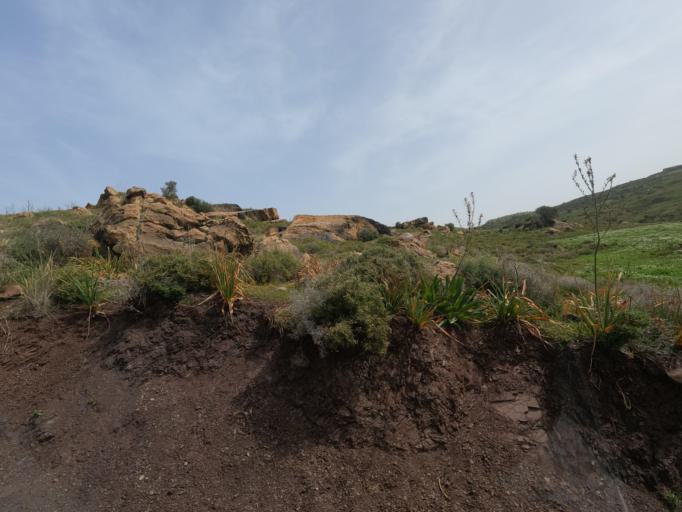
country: CY
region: Pafos
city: Pegeia
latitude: 34.9737
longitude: 32.3355
